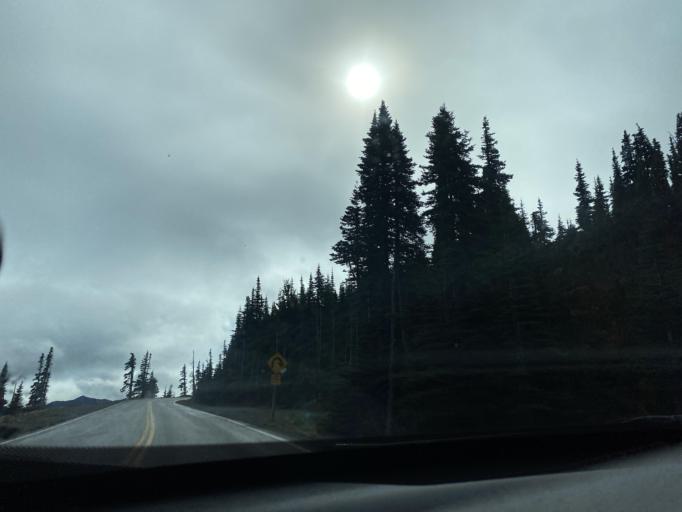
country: US
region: Washington
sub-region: Clallam County
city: Port Angeles
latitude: 47.9707
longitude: -123.4874
